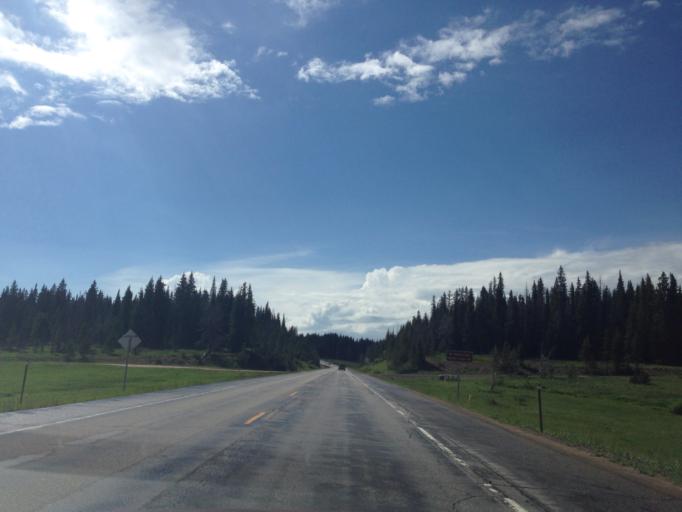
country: US
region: Colorado
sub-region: Routt County
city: Steamboat Springs
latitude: 40.3850
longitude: -106.6175
